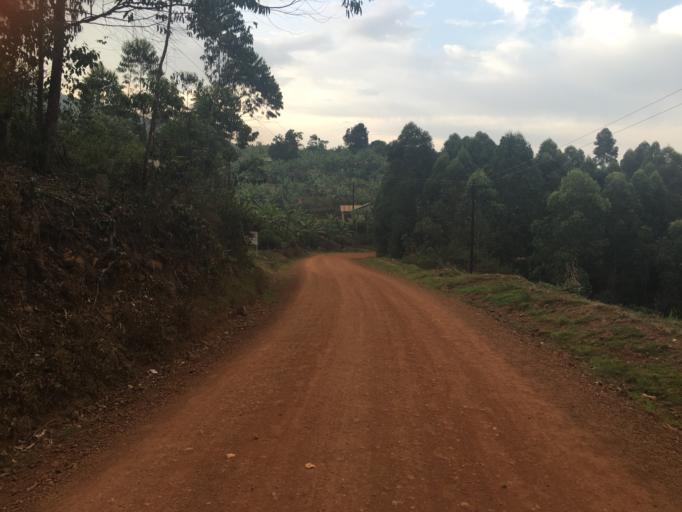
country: UG
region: Western Region
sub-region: Kanungu District
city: Ntungamo
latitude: -0.9784
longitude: 29.6173
